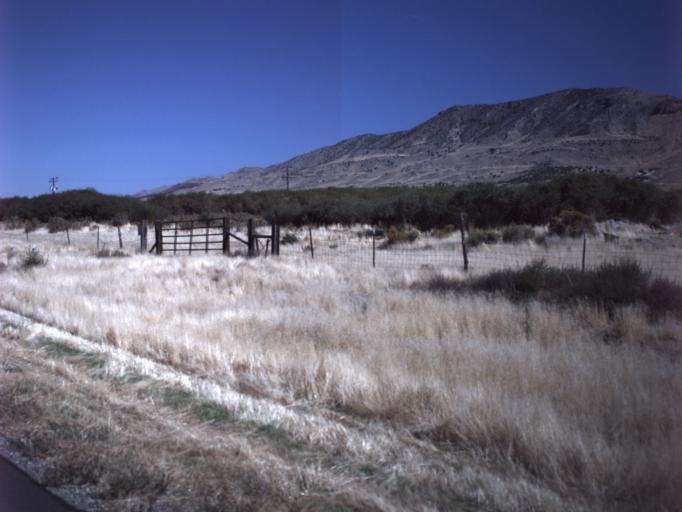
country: US
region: Utah
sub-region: Tooele County
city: Grantsville
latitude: 40.5269
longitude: -112.7477
